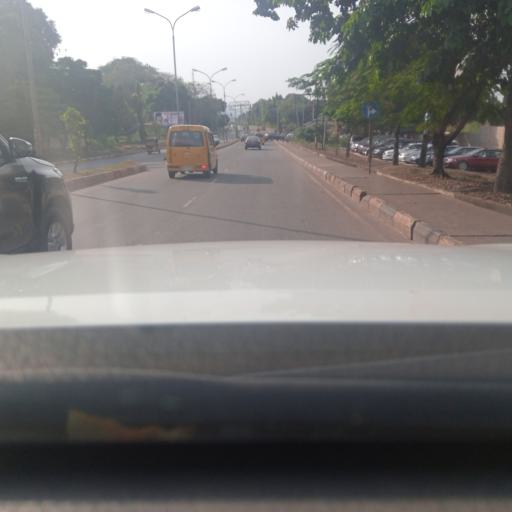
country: NG
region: Enugu
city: Enugu
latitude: 6.4401
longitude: 7.5148
